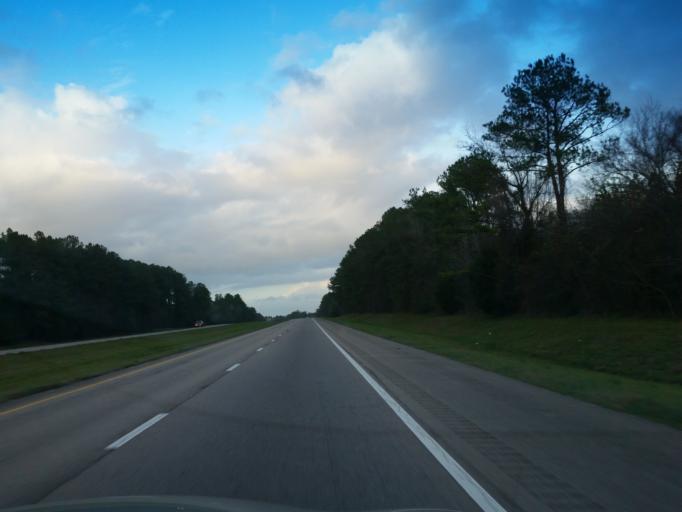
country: US
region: Mississippi
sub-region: Clarke County
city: Stonewall
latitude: 32.0056
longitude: -88.9329
